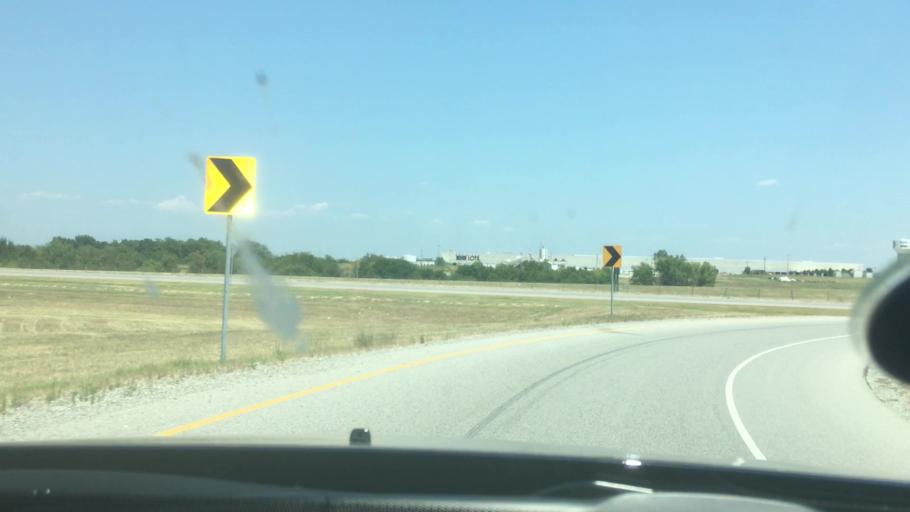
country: US
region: Oklahoma
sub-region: Bryan County
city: Calera
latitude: 33.9714
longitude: -96.4177
